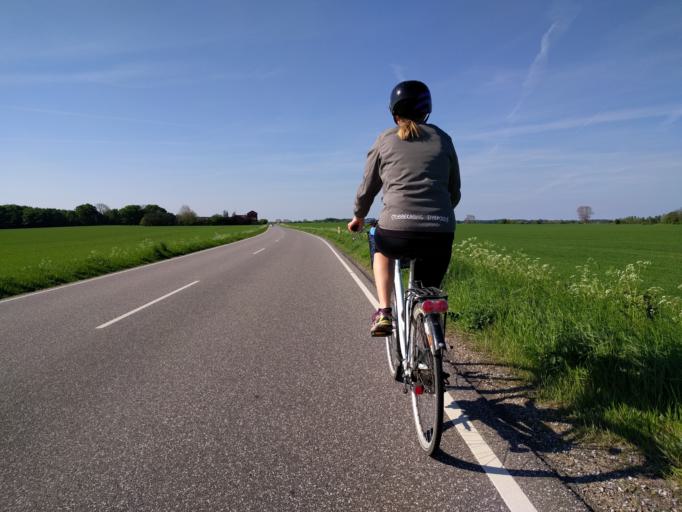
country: DK
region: Zealand
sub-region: Guldborgsund Kommune
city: Nykobing Falster
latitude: 54.7868
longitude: 11.9870
